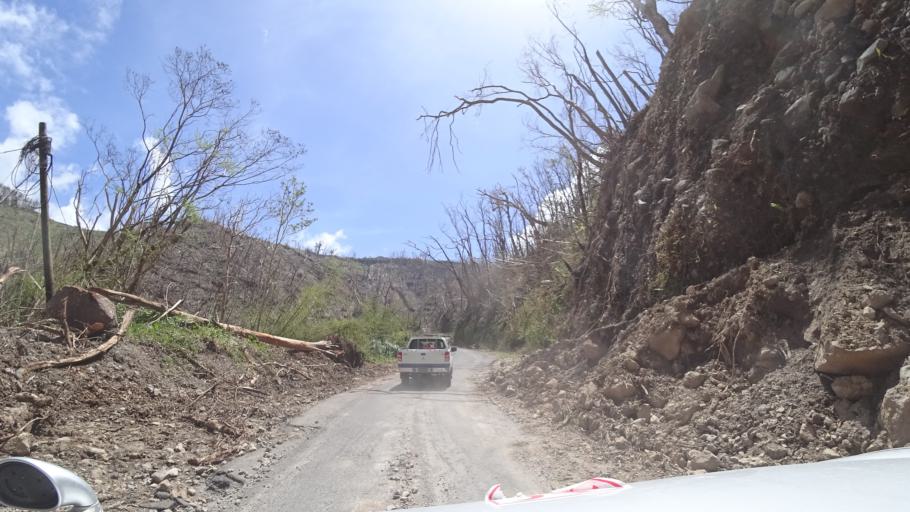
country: DM
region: Saint Luke
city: Pointe Michel
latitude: 15.2674
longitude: -61.3508
